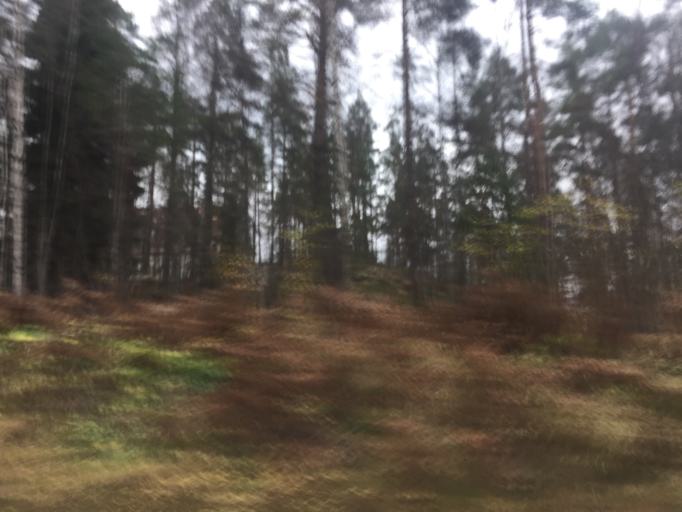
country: RU
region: Republic of Karelia
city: Lakhdenpokh'ya
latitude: 61.4321
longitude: 30.1434
